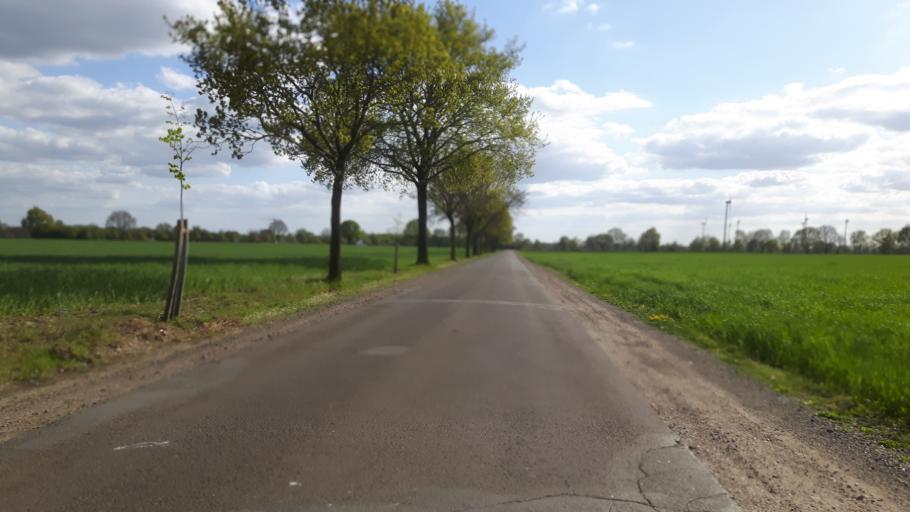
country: DE
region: Lower Saxony
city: Kirchseelte
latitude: 53.0029
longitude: 8.6922
